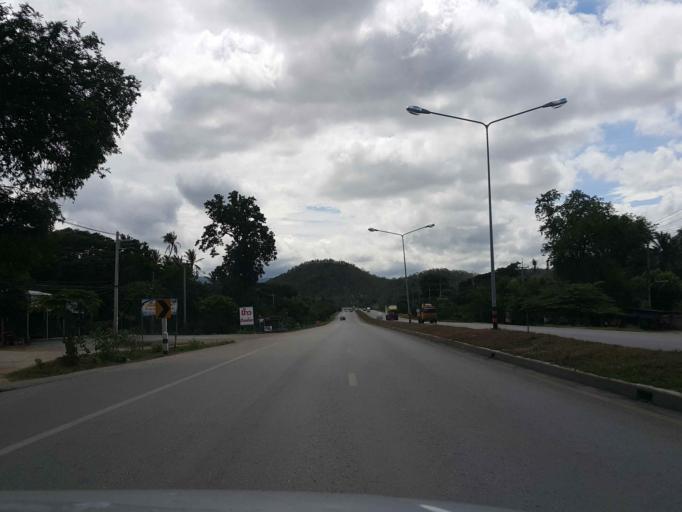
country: TH
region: Tak
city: Tak
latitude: 16.8209
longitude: 99.0769
